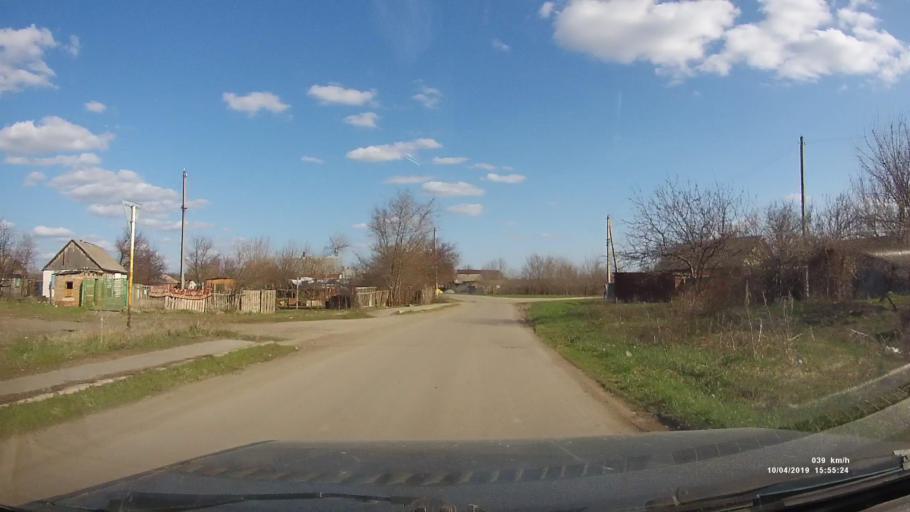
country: RU
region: Rostov
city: Masalovka
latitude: 48.4128
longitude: 40.2648
